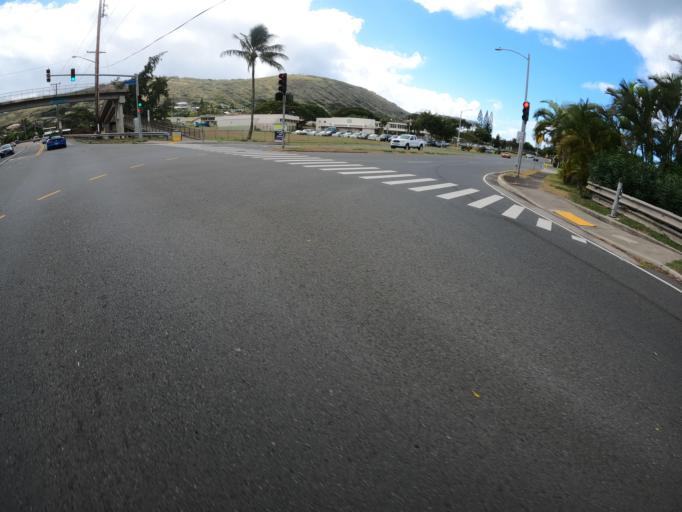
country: US
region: Hawaii
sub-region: Honolulu County
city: Waimanalo Beach
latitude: 21.2760
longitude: -157.7048
